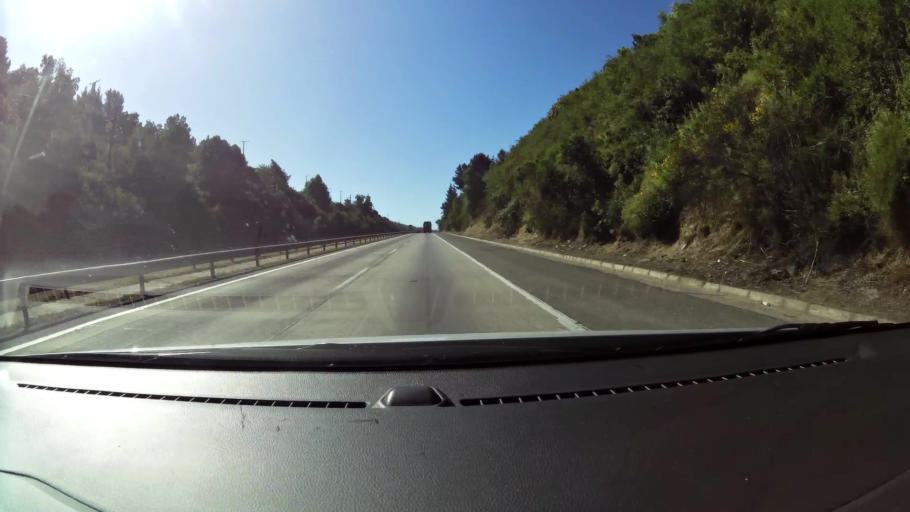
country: CL
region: Valparaiso
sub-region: Provincia de Marga Marga
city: Quilpue
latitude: -33.2353
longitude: -71.4609
